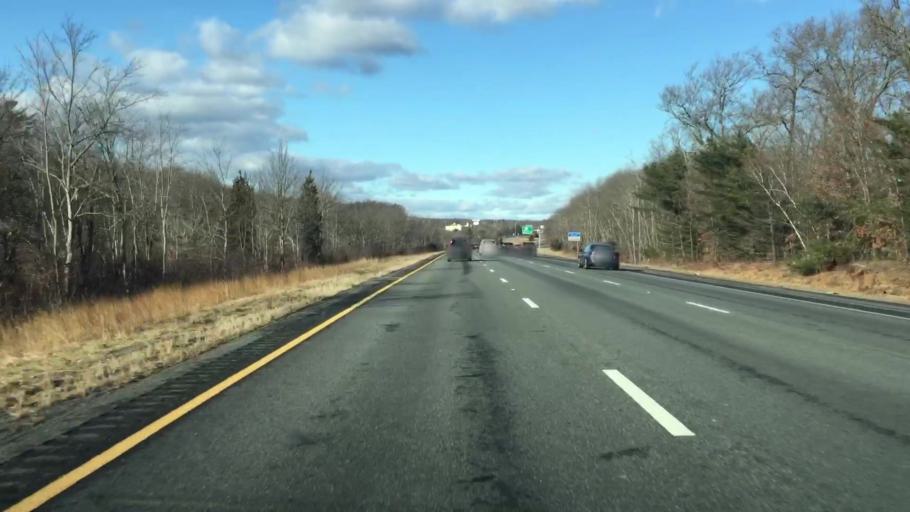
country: US
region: Massachusetts
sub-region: Worcester County
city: Milford
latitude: 42.1409
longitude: -71.4813
